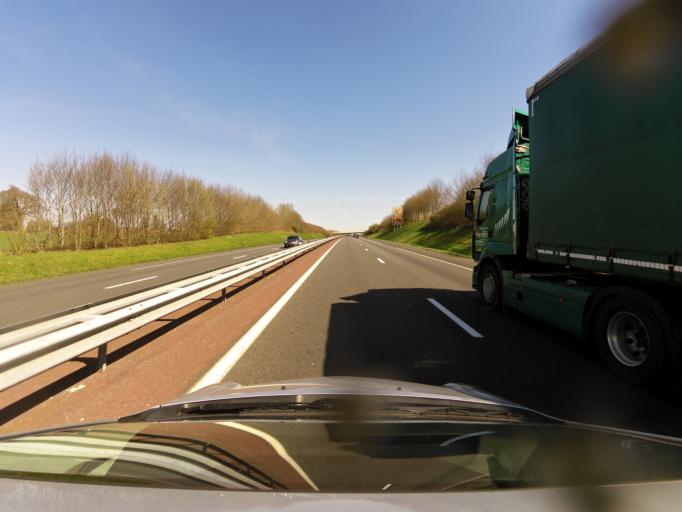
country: FR
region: Lower Normandy
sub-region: Departement de la Manche
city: Villedieu-les-Poeles
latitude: 48.8103
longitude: -1.2566
